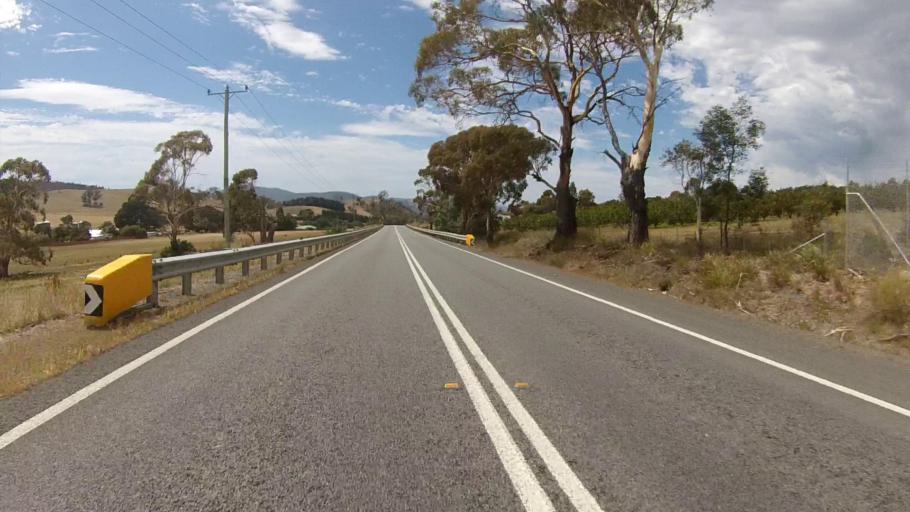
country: AU
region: Tasmania
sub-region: Brighton
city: Old Beach
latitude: -42.6689
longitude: 147.3801
